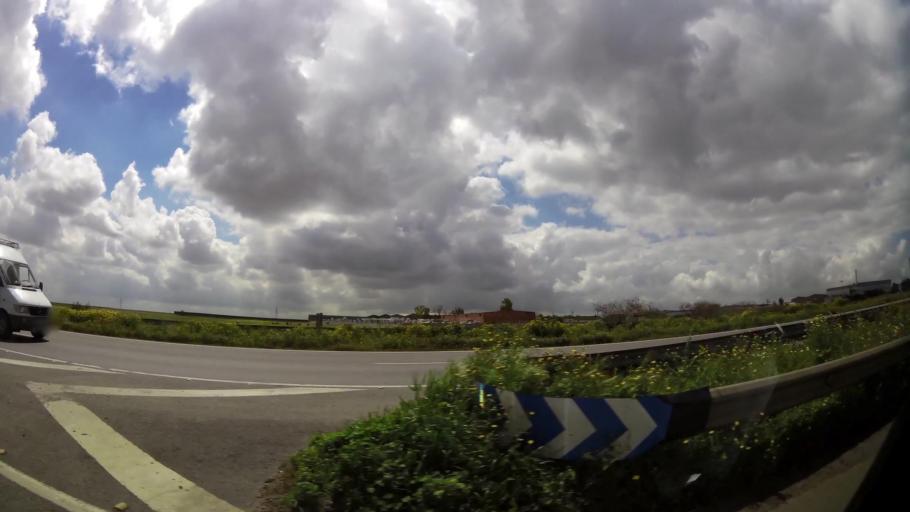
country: MA
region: Grand Casablanca
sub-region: Casablanca
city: Casablanca
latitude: 33.5299
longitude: -7.5638
